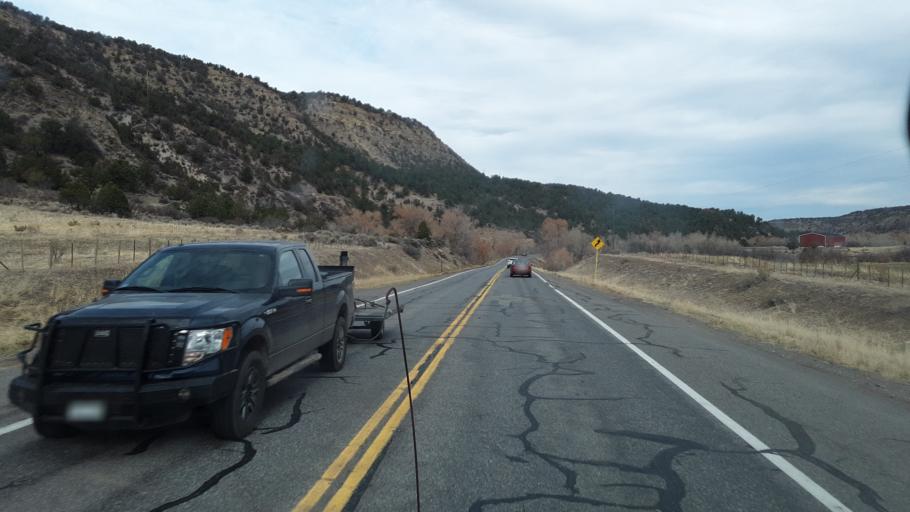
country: US
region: Colorado
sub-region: Montrose County
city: Montrose
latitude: 38.2707
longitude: -107.7646
